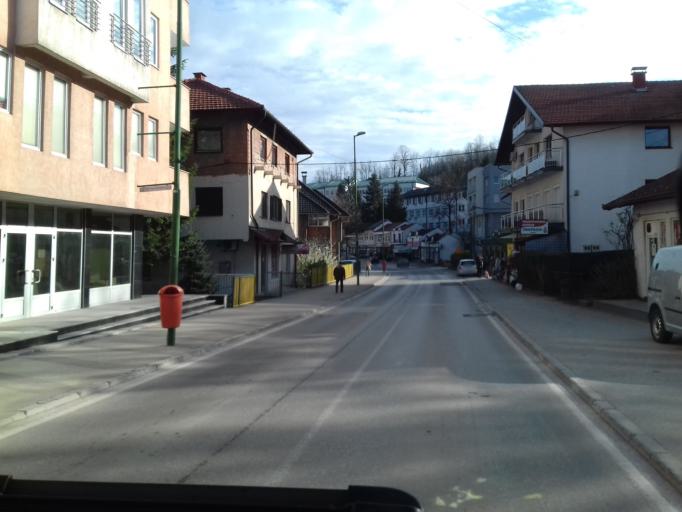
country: BA
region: Federation of Bosnia and Herzegovina
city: Tesanj
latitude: 44.6076
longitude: 17.9876
